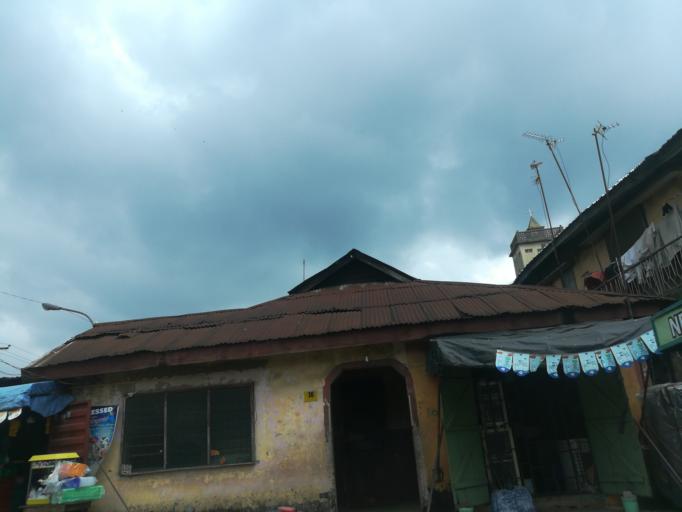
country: NG
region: Lagos
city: Mushin
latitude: 6.5267
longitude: 3.3661
